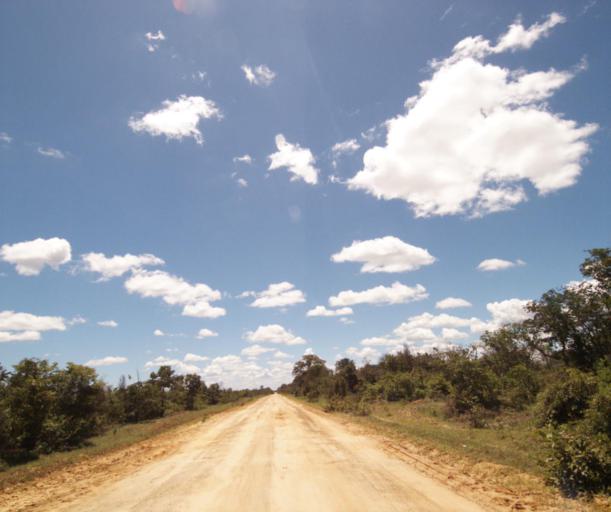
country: BR
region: Bahia
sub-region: Carinhanha
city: Carinhanha
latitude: -14.2091
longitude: -43.9954
